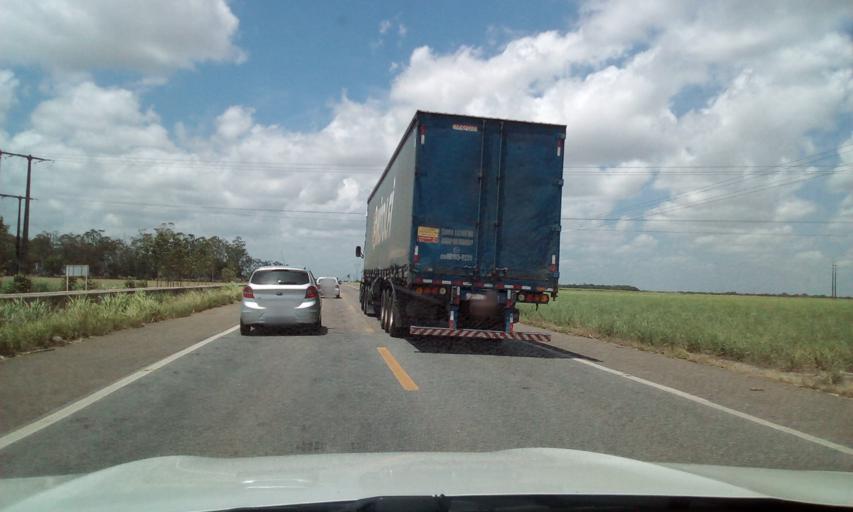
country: BR
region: Alagoas
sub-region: Campo Alegre
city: Campo Alegre
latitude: -9.9028
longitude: -36.2314
